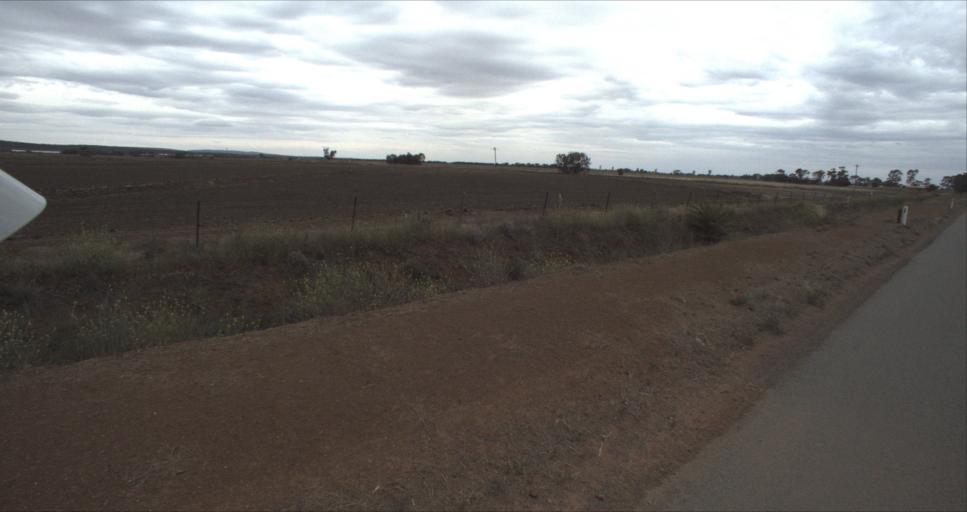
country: AU
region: New South Wales
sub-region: Leeton
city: Leeton
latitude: -34.4154
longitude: 146.3395
